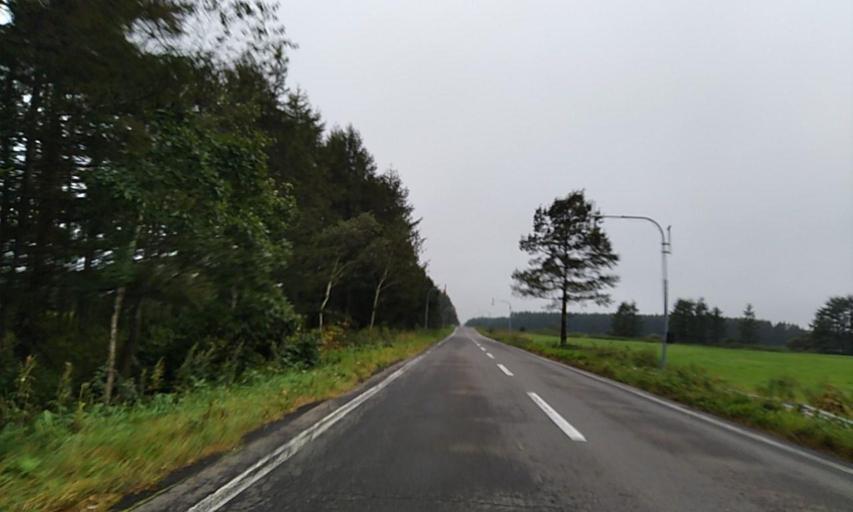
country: JP
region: Hokkaido
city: Shibetsu
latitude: 43.5246
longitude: 144.6913
